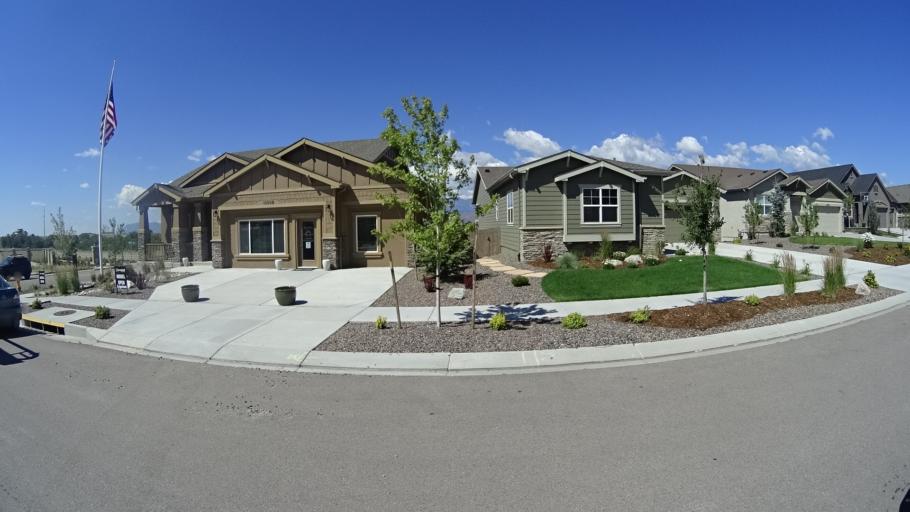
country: US
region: Colorado
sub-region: El Paso County
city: Black Forest
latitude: 38.9811
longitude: -104.7550
